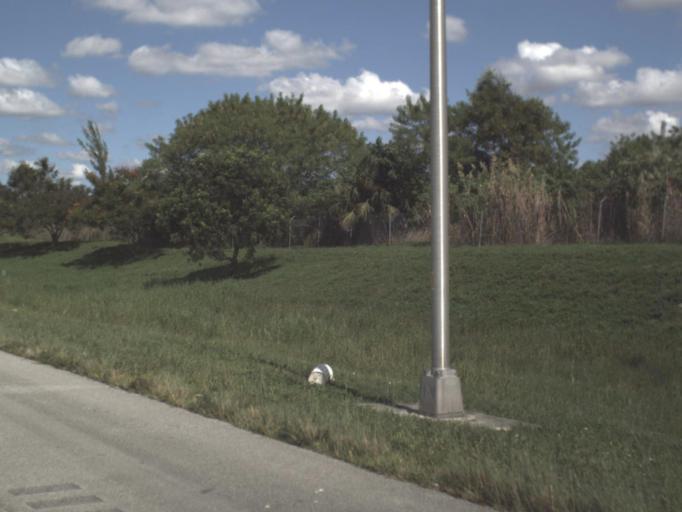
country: US
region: Florida
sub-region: Broward County
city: Coral Springs
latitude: 26.2810
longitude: -80.2970
